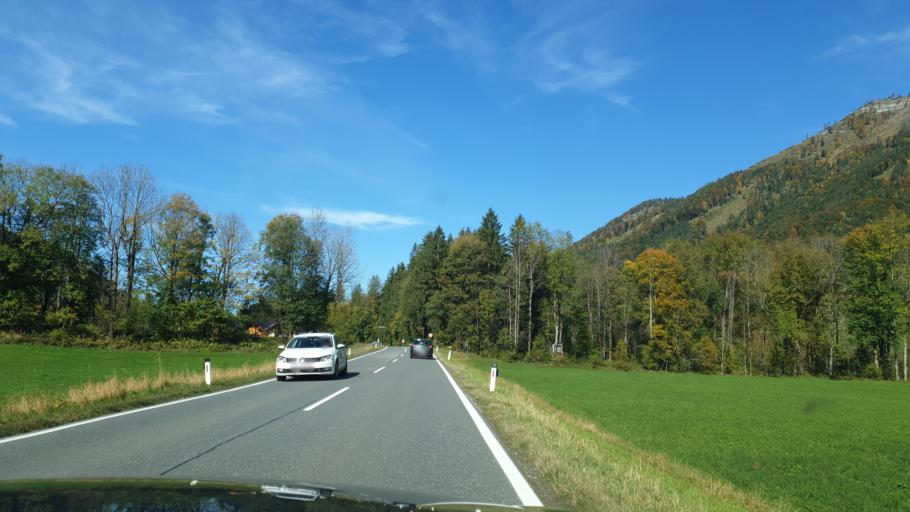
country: AT
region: Salzburg
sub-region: Politischer Bezirk Salzburg-Umgebung
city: Hintersee
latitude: 47.7341
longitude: 13.2651
